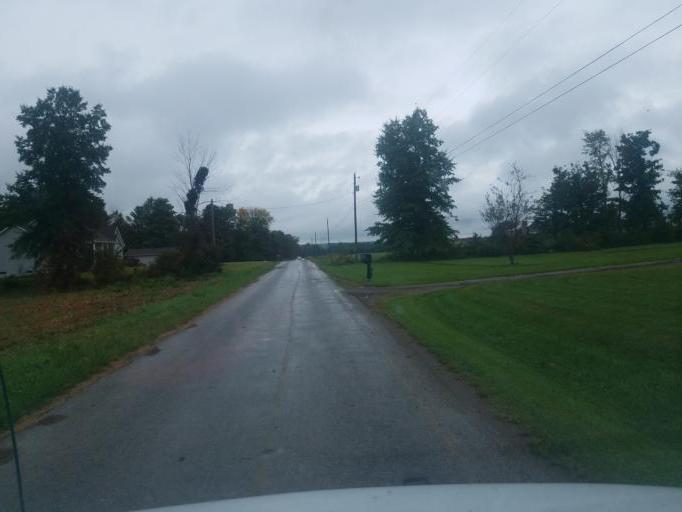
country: US
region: Ohio
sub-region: Wayne County
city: West Salem
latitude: 40.9301
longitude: -82.1465
